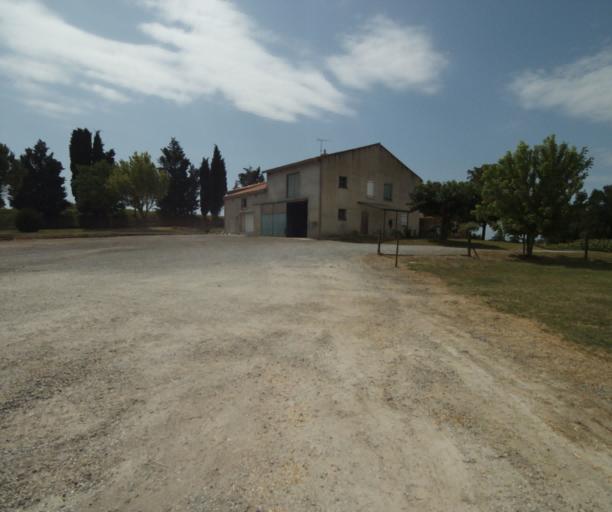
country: FR
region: Midi-Pyrenees
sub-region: Departement de la Haute-Garonne
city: Saint-Felix-Lauragais
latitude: 43.4276
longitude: 1.9096
